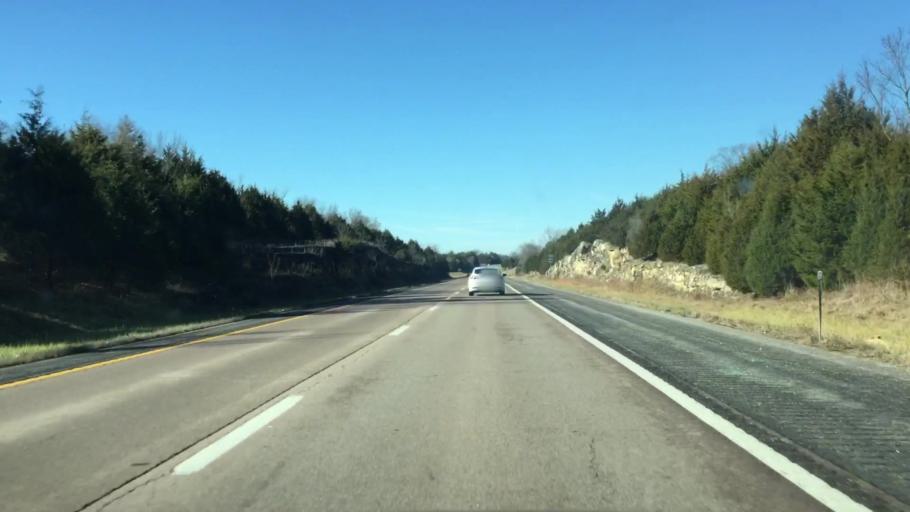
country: US
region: Missouri
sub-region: Miller County
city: Eldon
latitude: 38.3699
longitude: -92.4636
